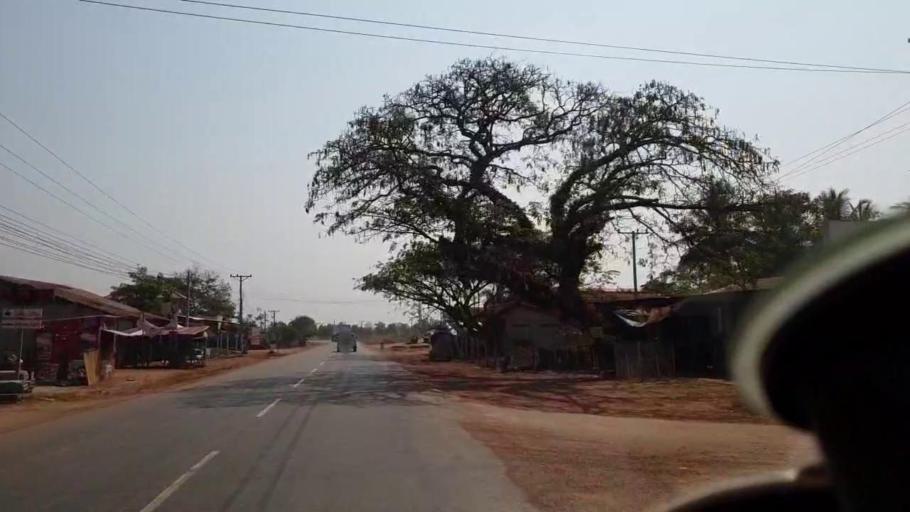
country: TH
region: Nong Khai
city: Phon Phisai
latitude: 18.0471
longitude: 102.8783
